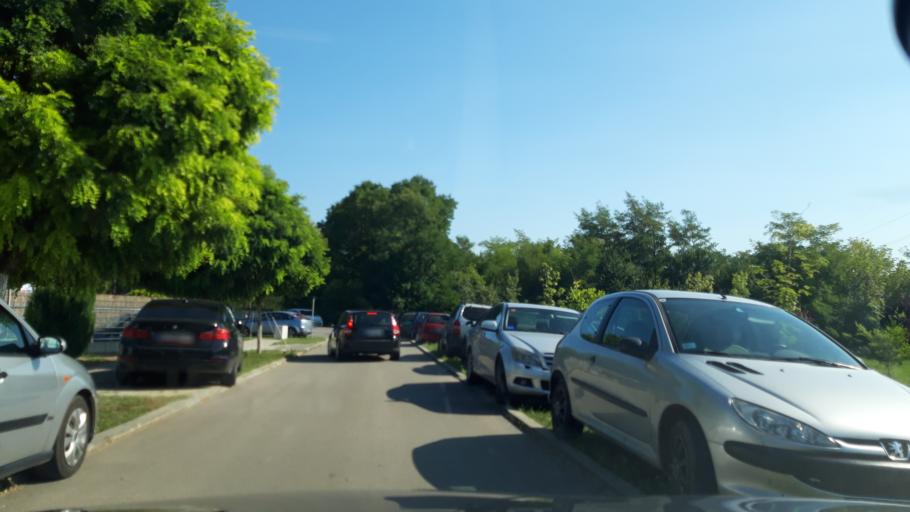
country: RS
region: Autonomna Pokrajina Vojvodina
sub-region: Sremski Okrug
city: Ruma
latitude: 45.0342
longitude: 19.8179
